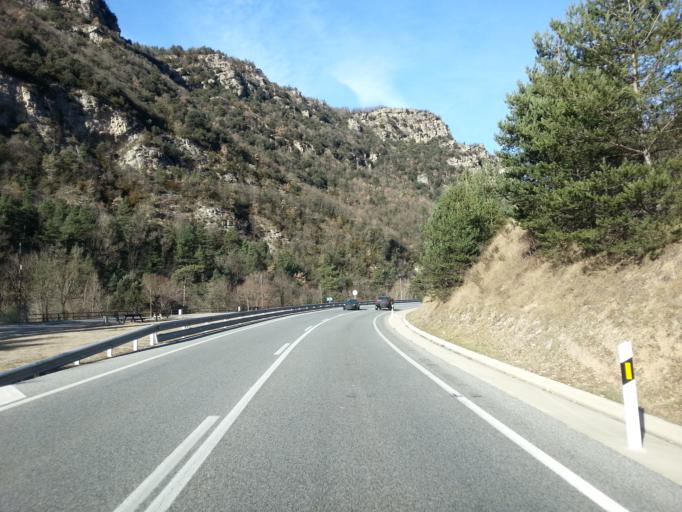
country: ES
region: Catalonia
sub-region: Provincia de Barcelona
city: Sant Julia de Cerdanyola
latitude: 42.2043
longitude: 1.8674
